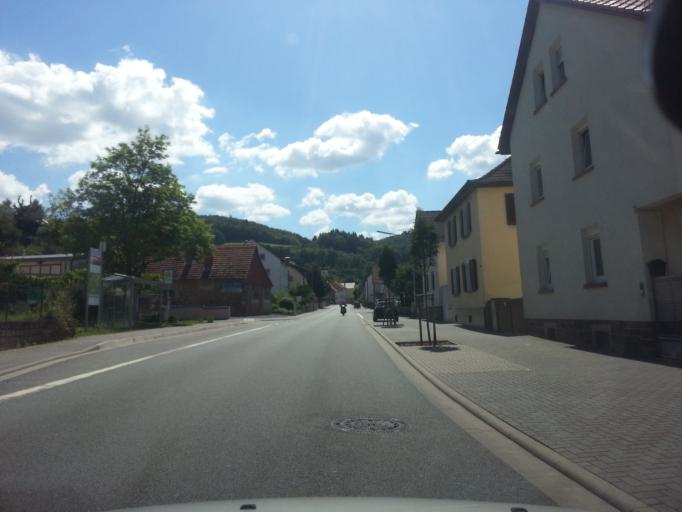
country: DE
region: Hesse
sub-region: Regierungsbezirk Darmstadt
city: Morlenbach
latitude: 49.5885
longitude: 8.7626
